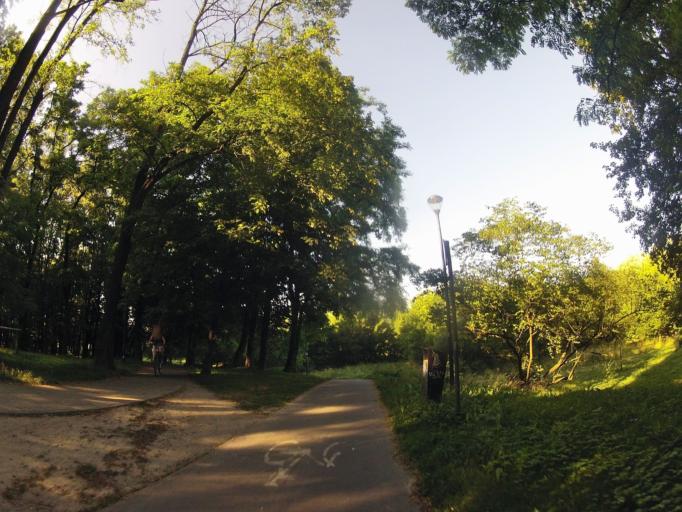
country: PL
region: Lesser Poland Voivodeship
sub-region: Krakow
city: Krakow
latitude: 50.0599
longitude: 19.9842
